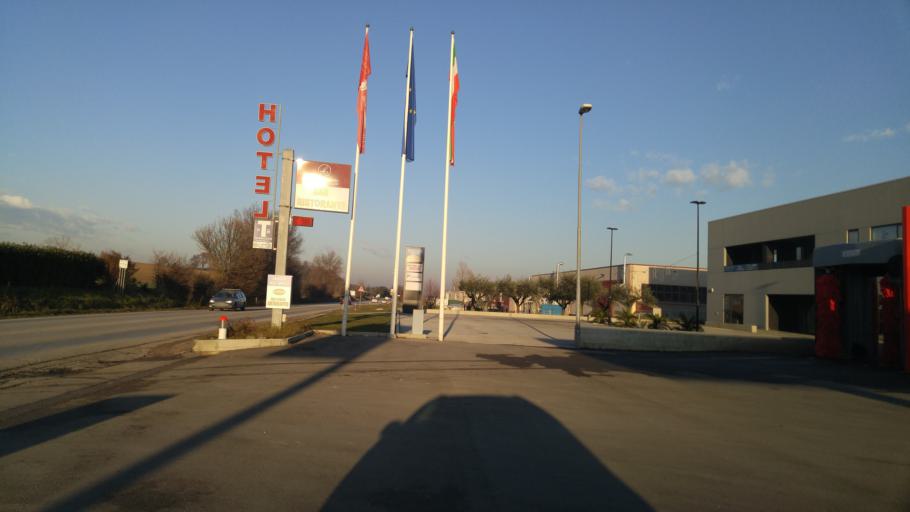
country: IT
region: The Marches
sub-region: Provincia di Pesaro e Urbino
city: Monte Porzio
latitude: 43.7029
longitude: 13.0659
